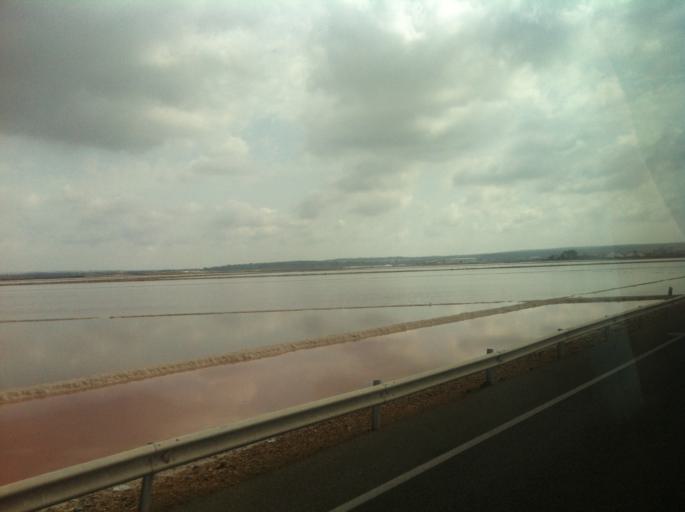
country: ES
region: Valencia
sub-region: Provincia de Alicante
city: Santa Pola
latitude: 38.1851
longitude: -0.6103
